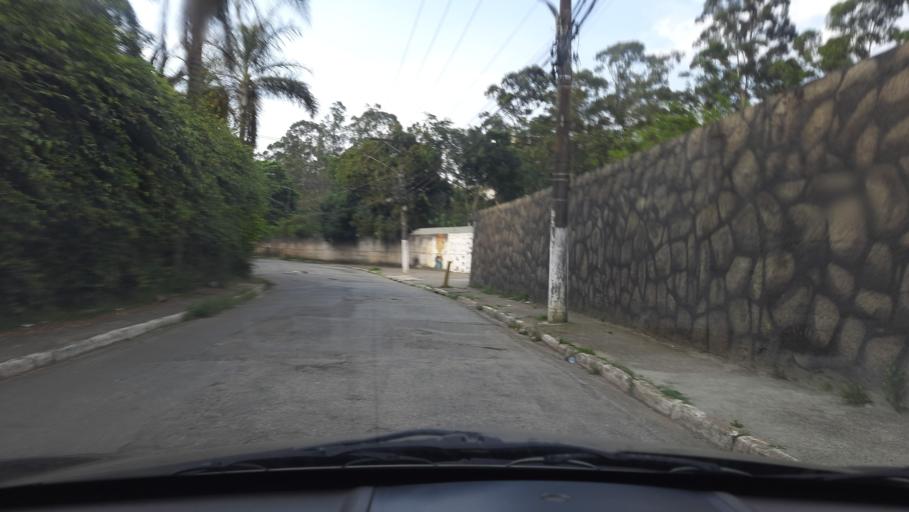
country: BR
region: Sao Paulo
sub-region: Caieiras
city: Caieiras
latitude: -23.4443
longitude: -46.7430
